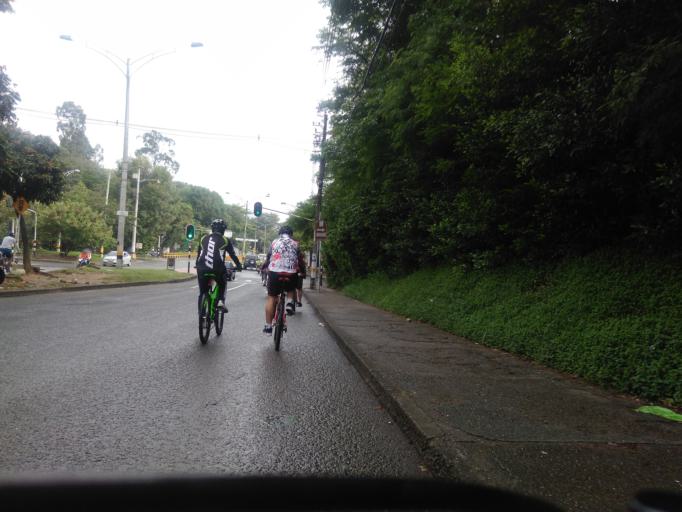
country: CO
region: Antioquia
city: Medellin
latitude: 6.2582
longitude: -75.5802
